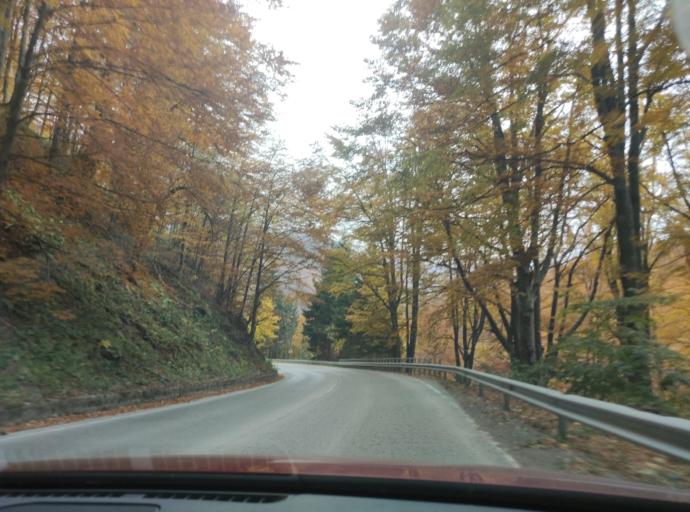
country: BG
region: Montana
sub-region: Obshtina Berkovitsa
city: Berkovitsa
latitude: 43.1358
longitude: 23.1477
